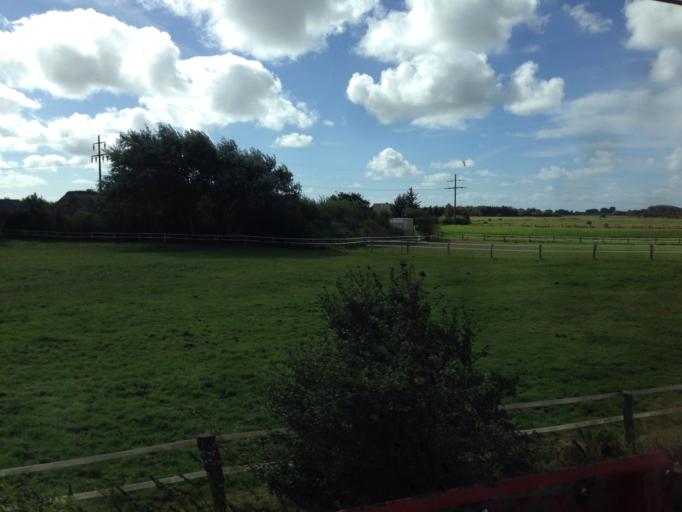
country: DE
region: Schleswig-Holstein
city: Sylt-Ost
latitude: 54.8750
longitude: 8.4134
